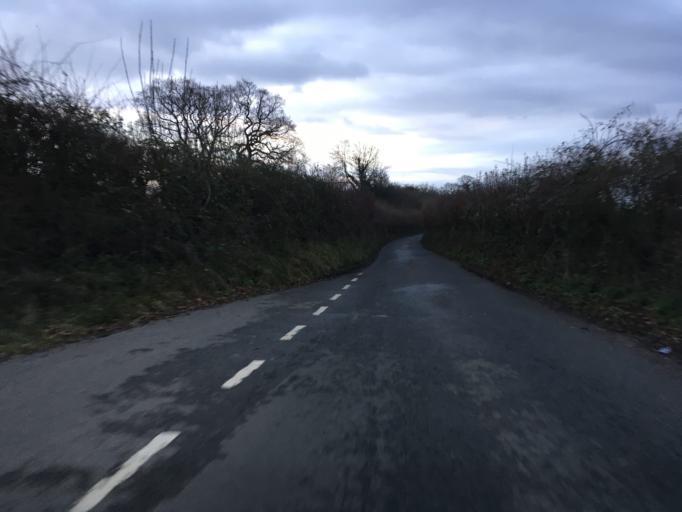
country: GB
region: Wales
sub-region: Newport
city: Bishton
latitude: 51.5943
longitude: -2.8789
